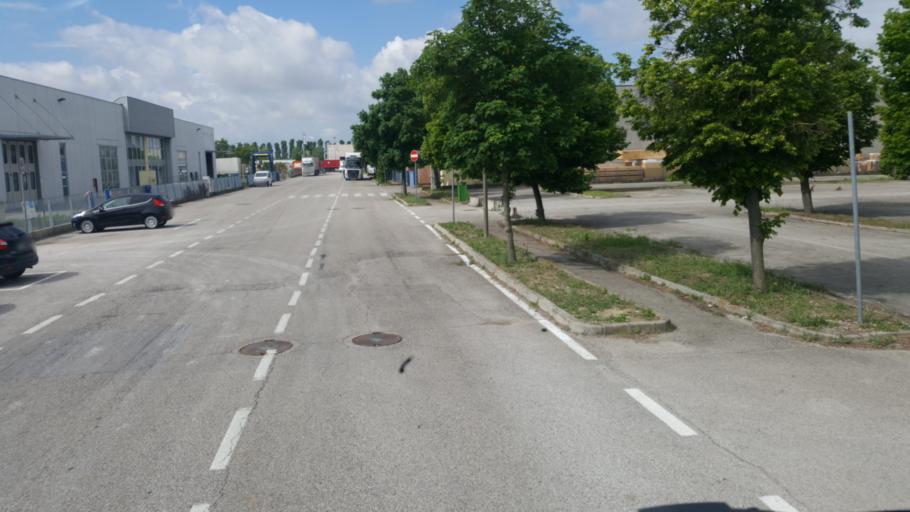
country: IT
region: Veneto
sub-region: Provincia di Venezia
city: Noventa di Piave
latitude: 45.6742
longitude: 12.5599
